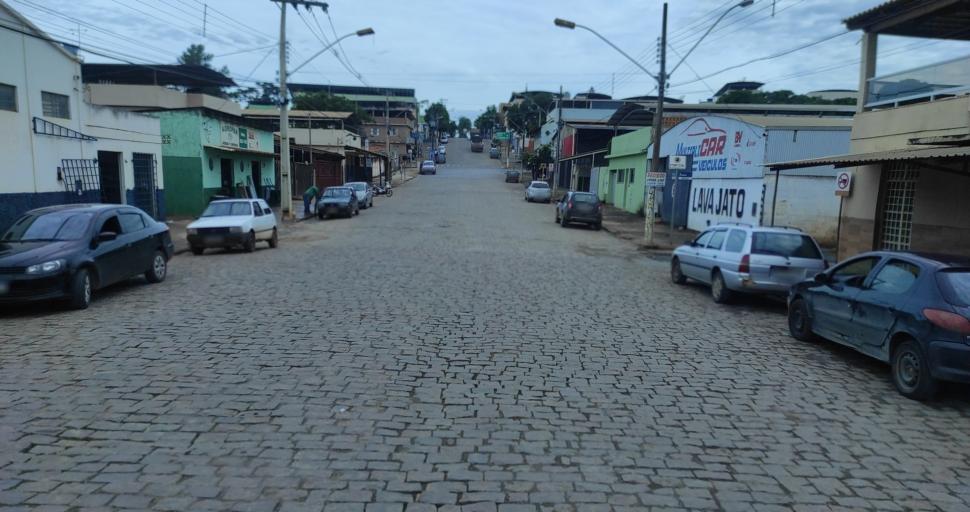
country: BR
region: Minas Gerais
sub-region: Arcos
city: Arcos
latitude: -20.3750
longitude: -45.6620
